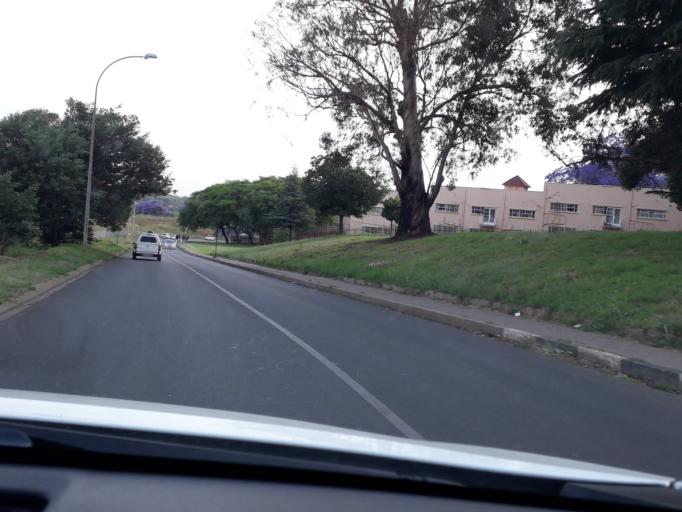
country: ZA
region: Gauteng
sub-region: City of Johannesburg Metropolitan Municipality
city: Johannesburg
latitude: -26.1693
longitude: 27.9748
